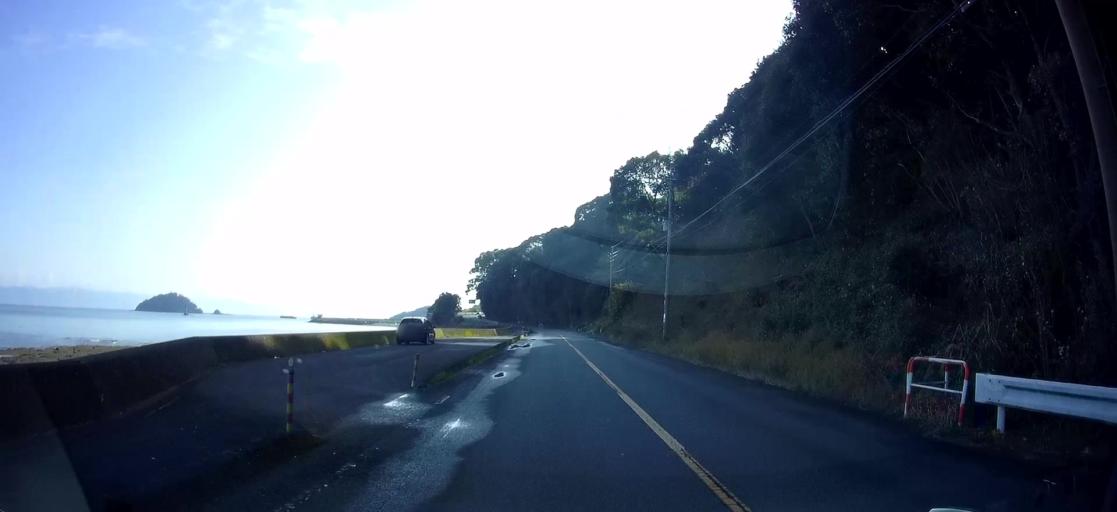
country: JP
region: Kumamoto
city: Yatsushiro
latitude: 32.4794
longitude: 130.4361
